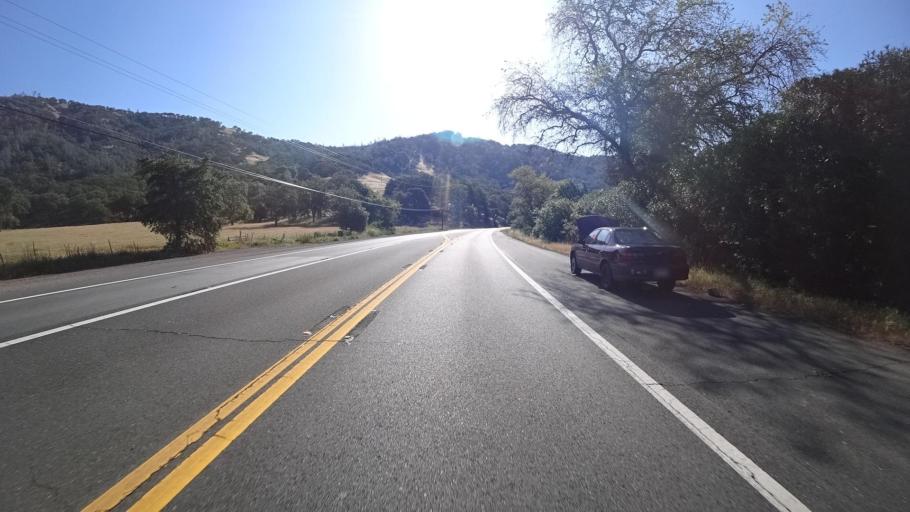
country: US
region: California
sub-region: Lake County
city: Soda Bay
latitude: 39.0432
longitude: -122.7534
